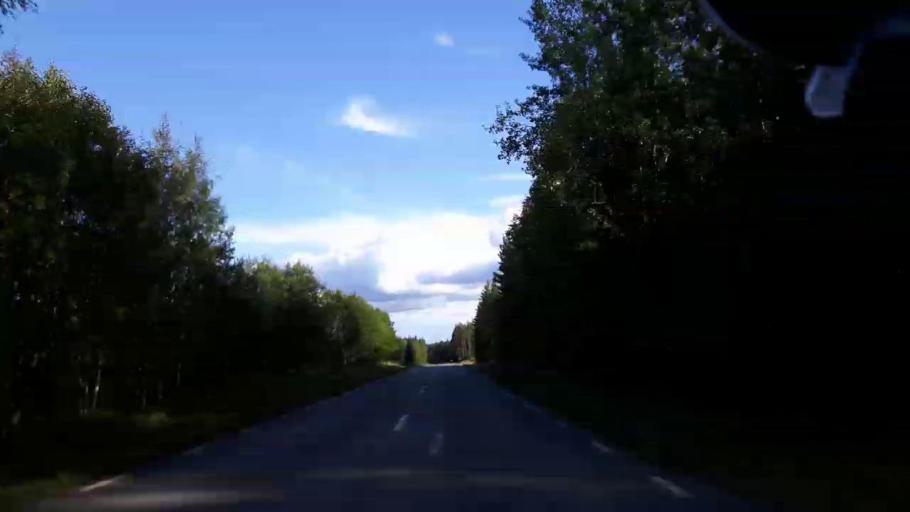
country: SE
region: Jaemtland
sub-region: Stroemsunds Kommun
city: Stroemsund
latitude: 63.4023
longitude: 15.5724
